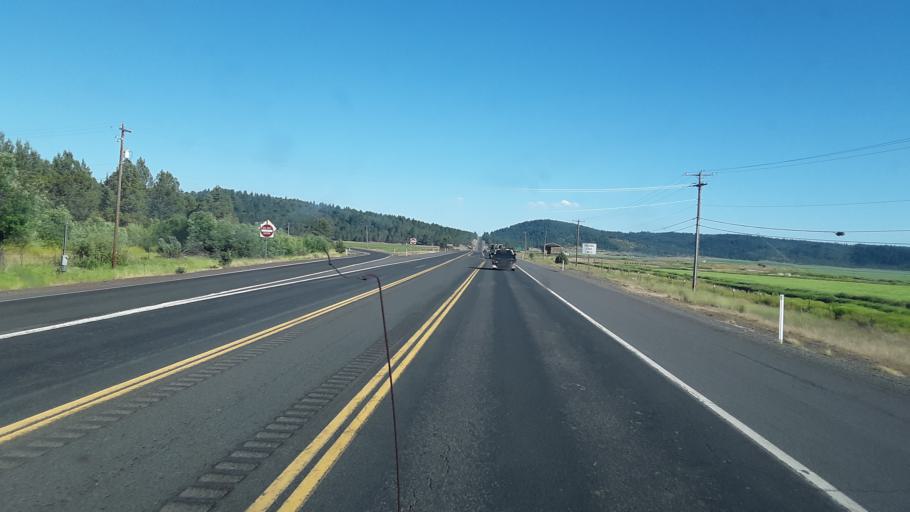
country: US
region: Oregon
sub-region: Klamath County
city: Klamath Falls
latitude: 42.2600
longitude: -121.8748
